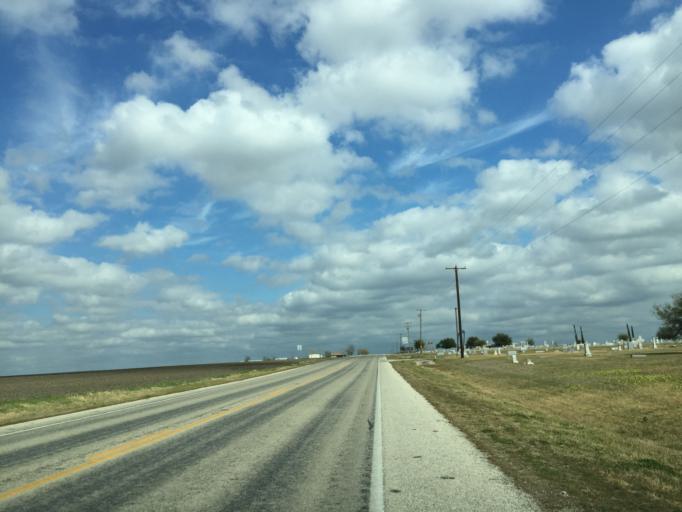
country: US
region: Texas
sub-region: Williamson County
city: Granger
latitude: 30.7191
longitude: -97.4282
